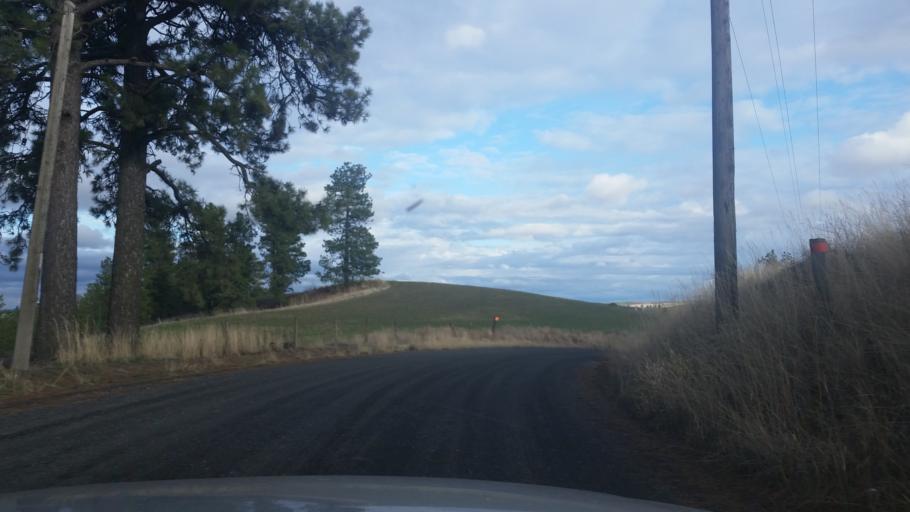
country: US
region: Washington
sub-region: Spokane County
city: Cheney
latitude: 47.4275
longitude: -117.4241
